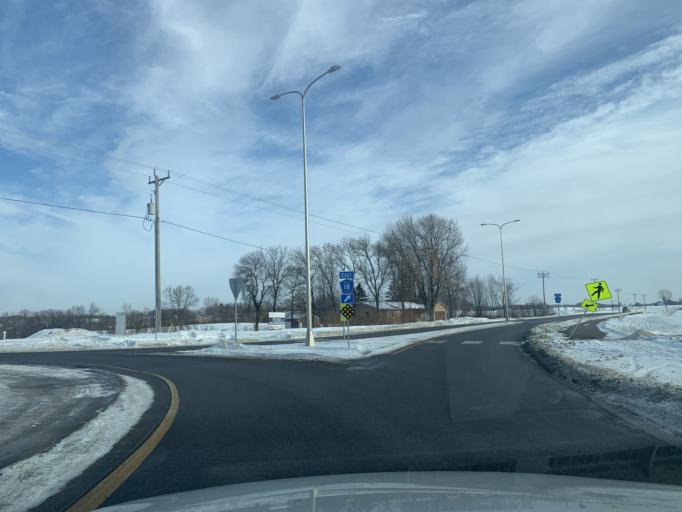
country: US
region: Minnesota
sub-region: Wright County
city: Albertville
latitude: 45.2241
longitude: -93.6438
